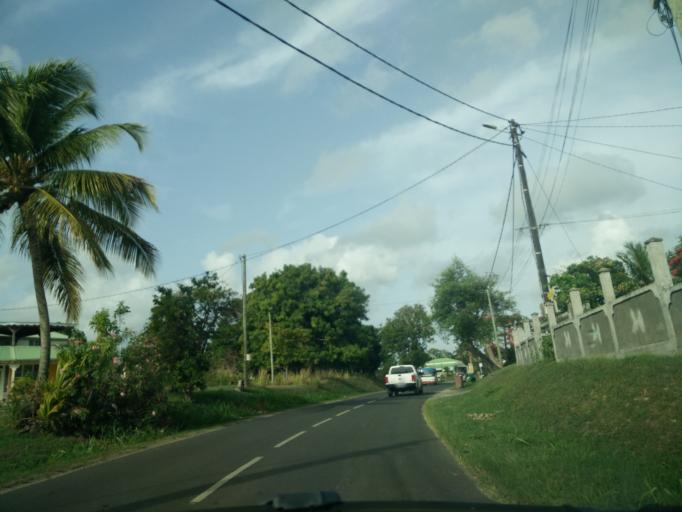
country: GP
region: Guadeloupe
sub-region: Guadeloupe
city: Le Moule
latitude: 16.3014
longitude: -61.3663
